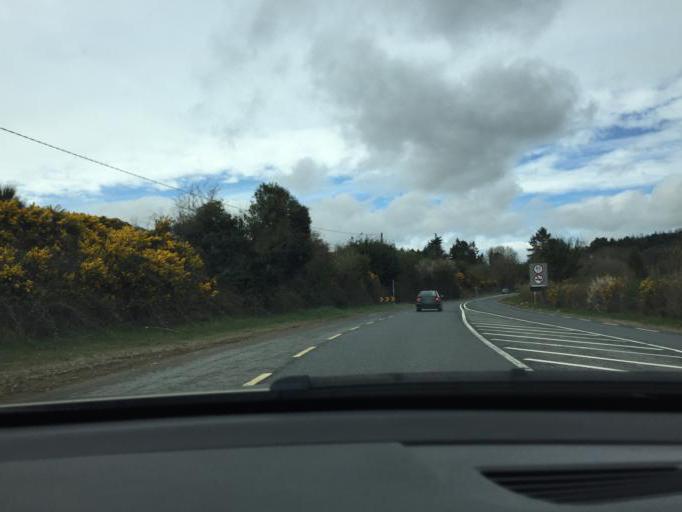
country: IE
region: Leinster
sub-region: Wicklow
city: Rathnew
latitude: 52.9253
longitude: -6.1164
